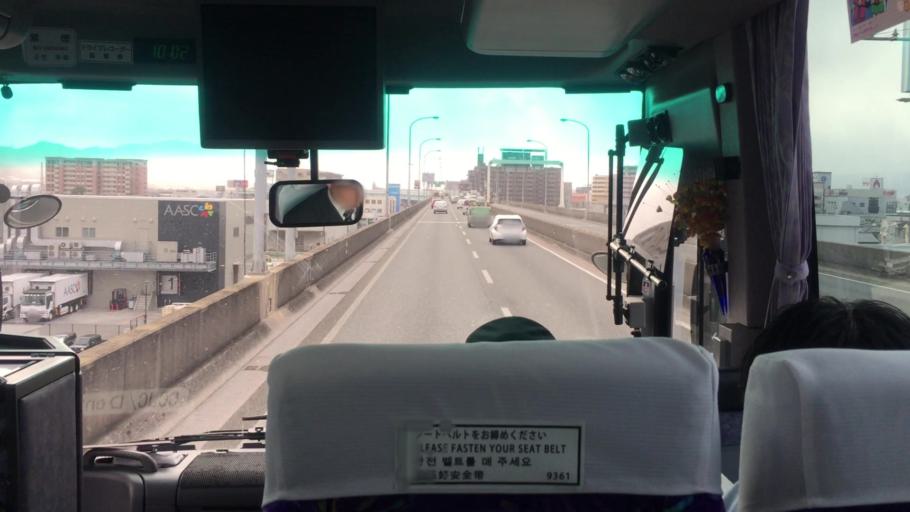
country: JP
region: Fukuoka
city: Fukuoka-shi
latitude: 33.5809
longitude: 130.4434
